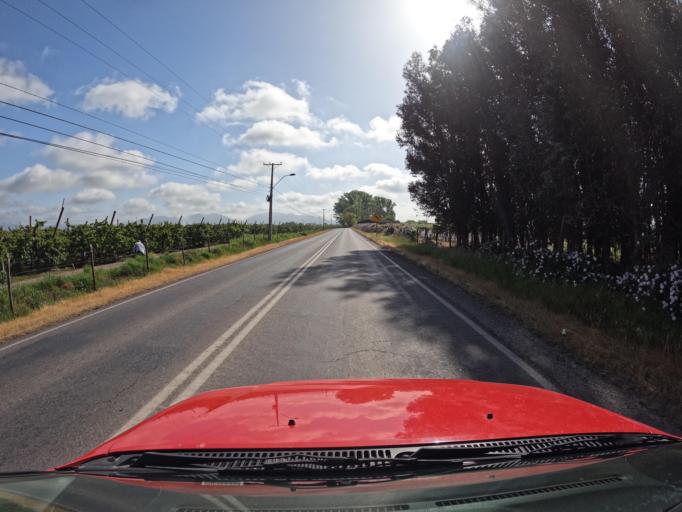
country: CL
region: Maule
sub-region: Provincia de Curico
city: Rauco
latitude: -34.9009
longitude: -71.2751
